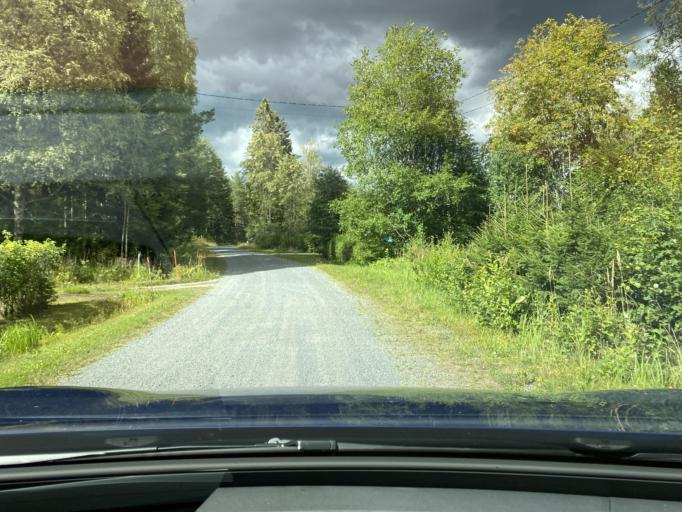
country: FI
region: Pirkanmaa
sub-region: Lounais-Pirkanmaa
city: Vammala
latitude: 61.2999
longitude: 22.9280
